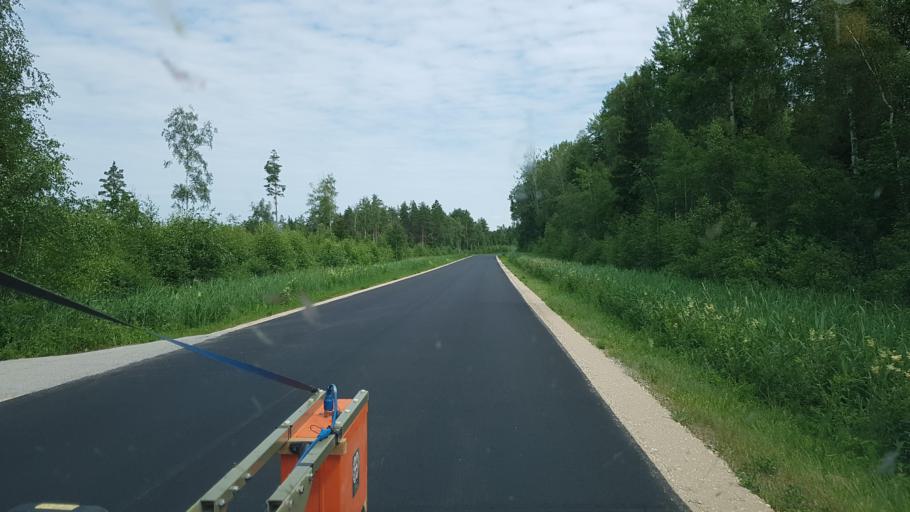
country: EE
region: Paernumaa
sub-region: Audru vald
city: Audru
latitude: 58.6175
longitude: 24.2291
